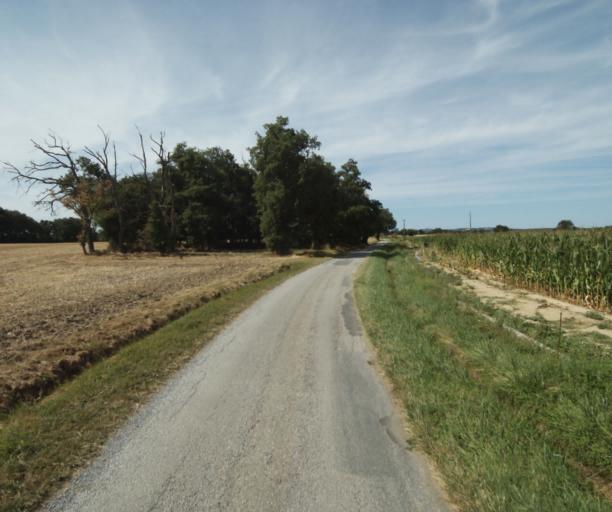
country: FR
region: Midi-Pyrenees
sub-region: Departement du Tarn
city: Soreze
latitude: 43.5034
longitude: 2.0633
